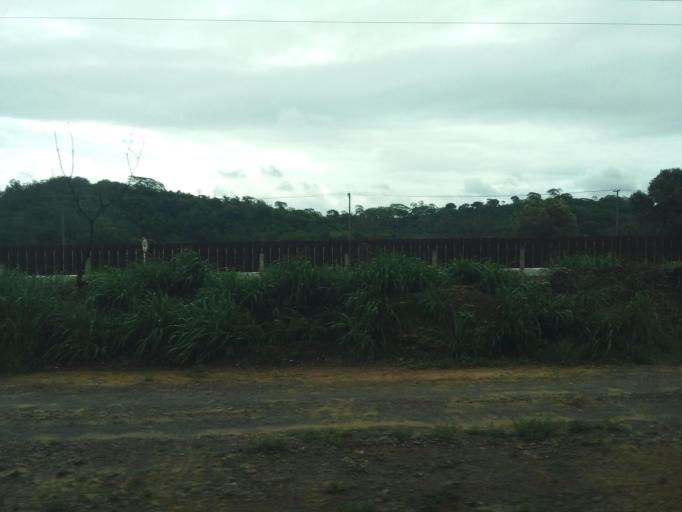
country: BR
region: Minas Gerais
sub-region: Ipatinga
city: Ipatinga
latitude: -19.4796
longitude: -42.4902
